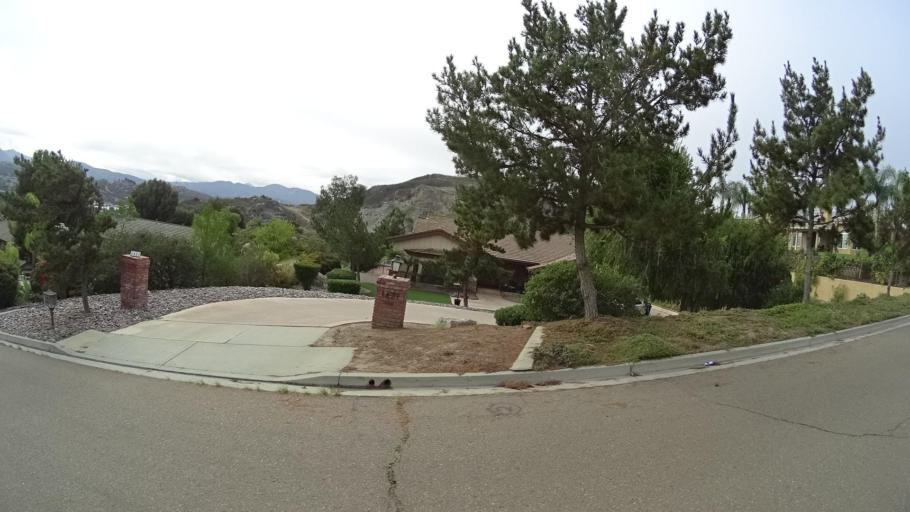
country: US
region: California
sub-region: San Diego County
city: Rancho San Diego
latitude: 32.7627
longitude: -116.9306
